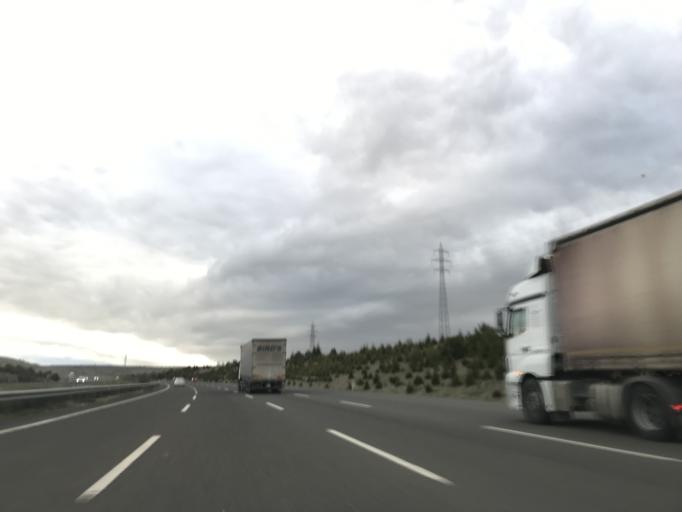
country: TR
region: Ankara
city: Etimesgut
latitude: 39.8050
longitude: 32.6440
